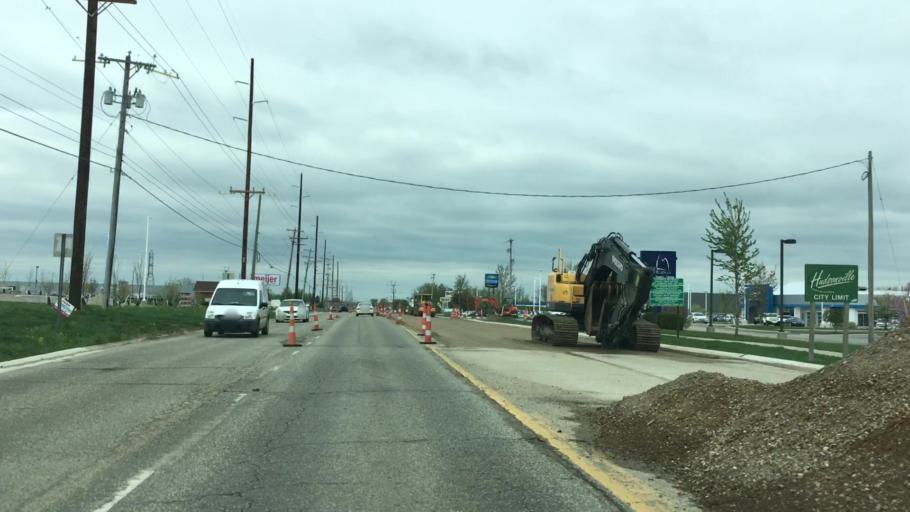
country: US
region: Michigan
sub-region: Ottawa County
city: Hudsonville
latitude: 42.8420
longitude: -85.8618
